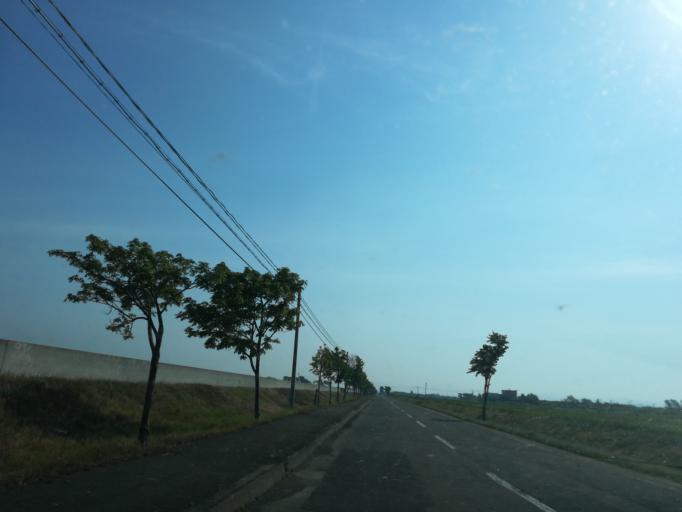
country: JP
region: Hokkaido
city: Iwamizawa
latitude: 43.1622
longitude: 141.6889
